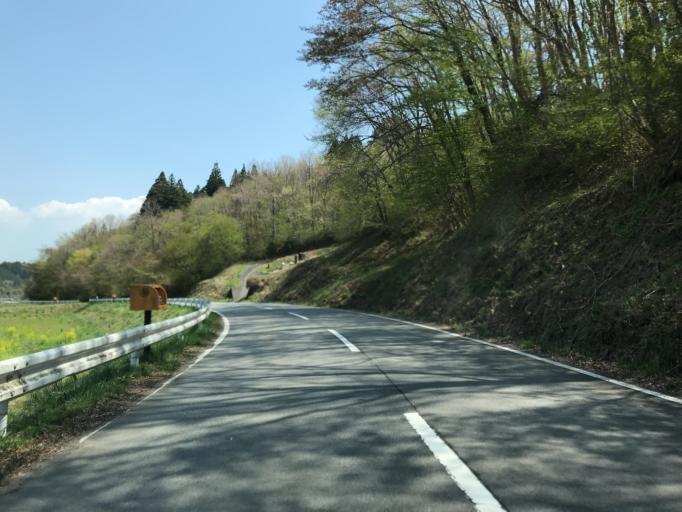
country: JP
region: Ibaraki
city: Kitaibaraki
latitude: 36.9690
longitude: 140.6503
